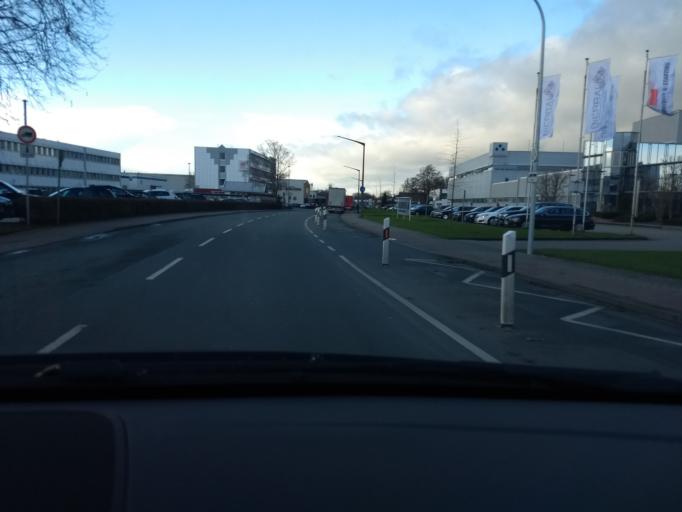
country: DE
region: North Rhine-Westphalia
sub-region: Regierungsbezirk Munster
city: Borken
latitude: 51.8477
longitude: 6.8729
